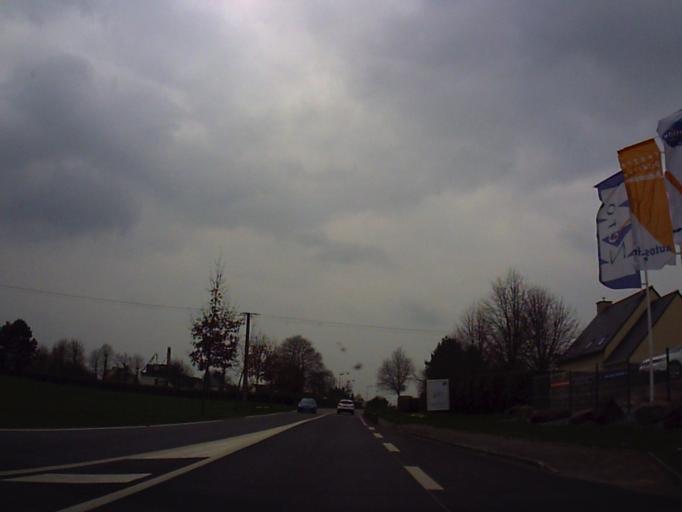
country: FR
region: Brittany
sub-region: Departement d'Ille-et-Vilaine
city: Breteil
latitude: 48.1440
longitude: -1.8900
